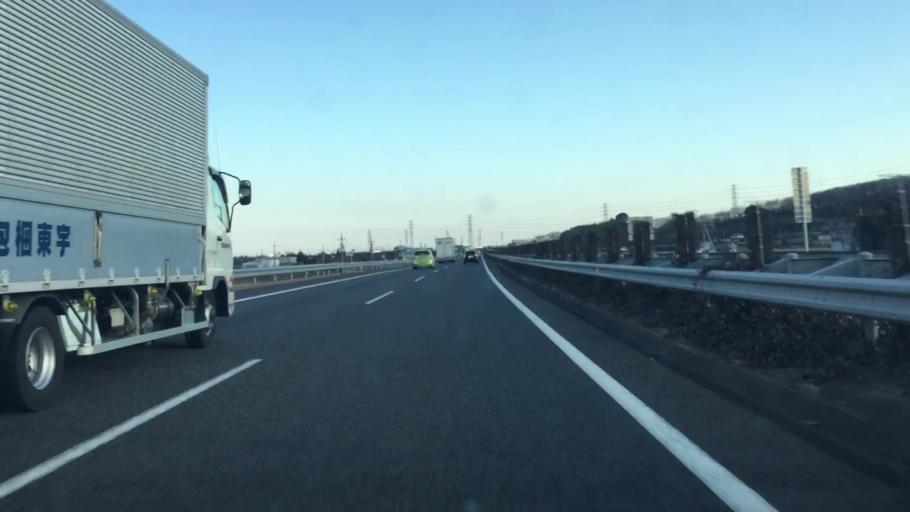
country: JP
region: Gunma
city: Ota
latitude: 36.3350
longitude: 139.3714
